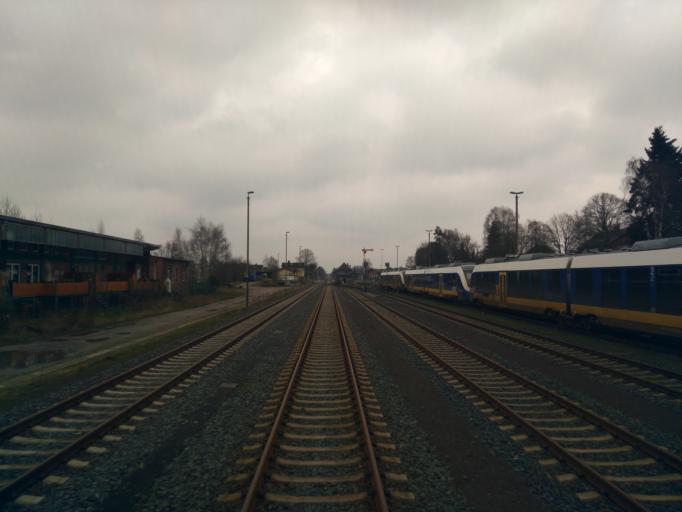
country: DE
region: Lower Saxony
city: Soltau
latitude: 52.9839
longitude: 9.8265
